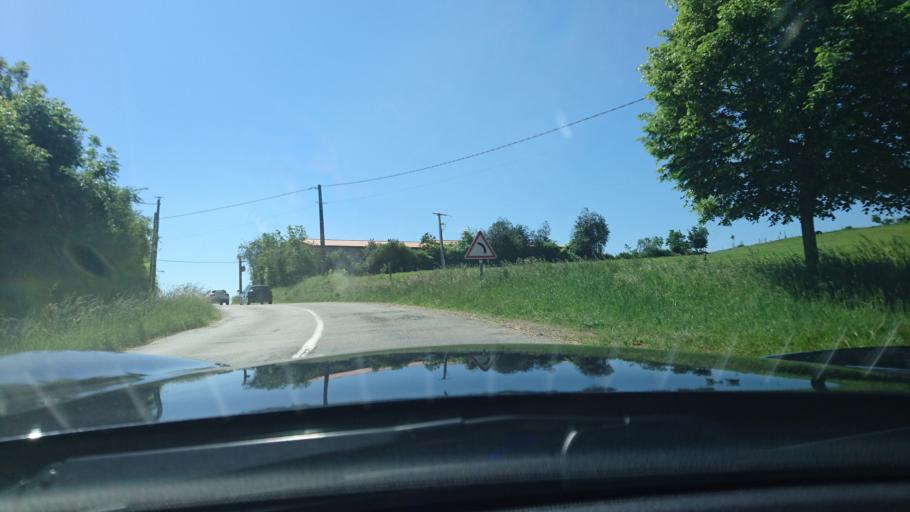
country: FR
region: Rhone-Alpes
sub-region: Departement de la Loire
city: Bussieres
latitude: 45.8440
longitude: 4.2642
